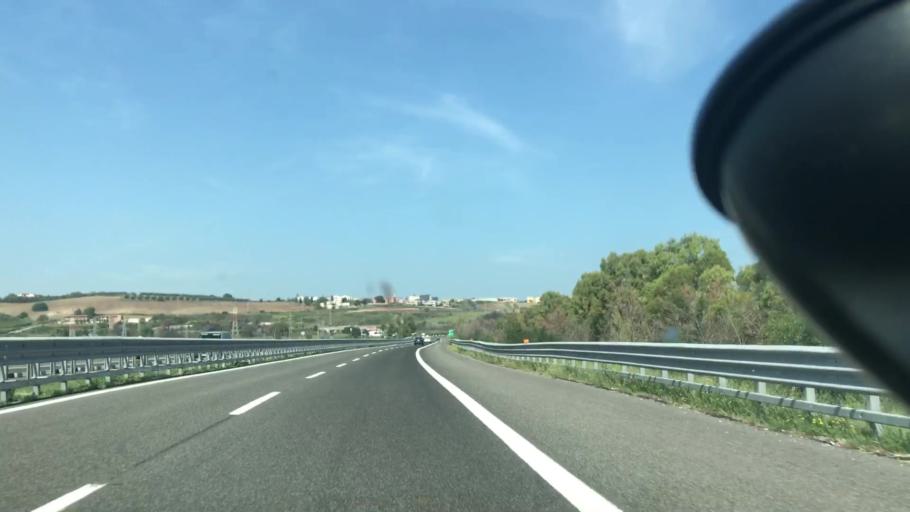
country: IT
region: Molise
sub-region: Provincia di Campobasso
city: Campomarino
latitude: 41.9592
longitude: 15.0070
